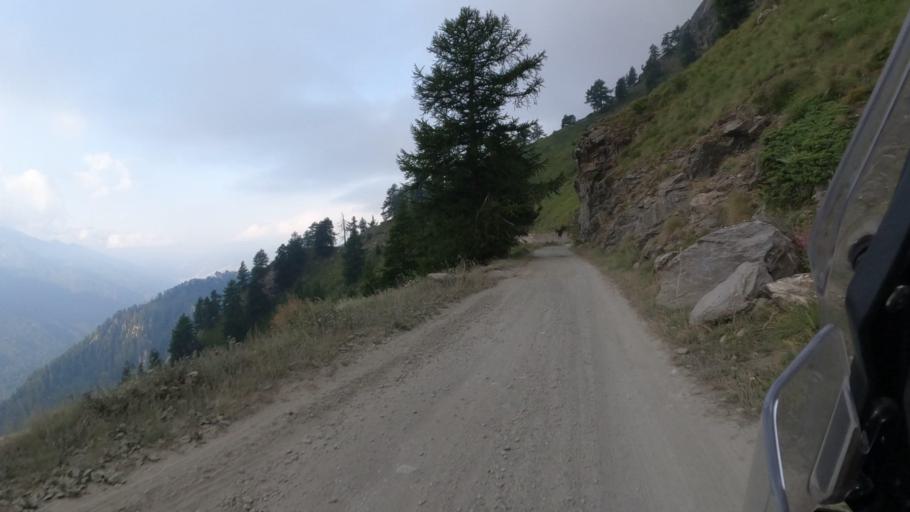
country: IT
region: Piedmont
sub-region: Provincia di Torino
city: Usseaux
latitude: 45.0602
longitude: 6.9926
